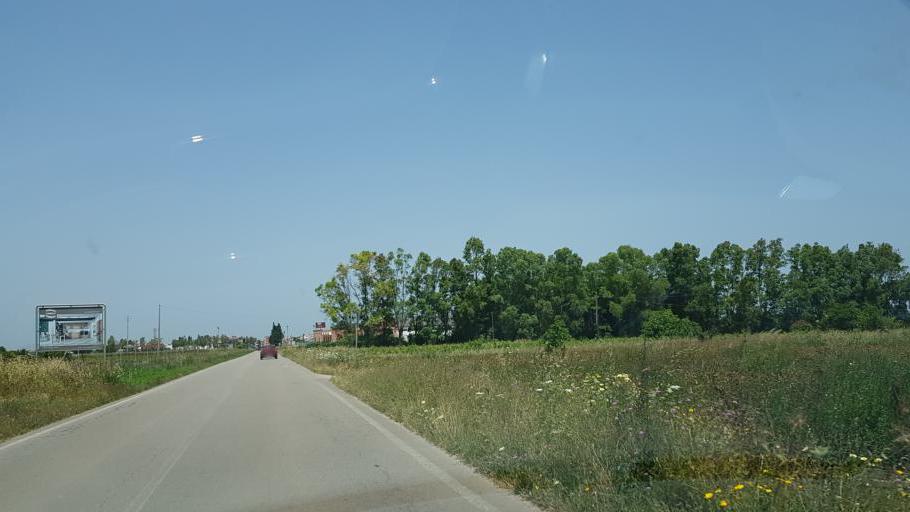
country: IT
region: Apulia
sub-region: Provincia di Brindisi
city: San Pancrazio Salentino
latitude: 40.4042
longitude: 17.8358
